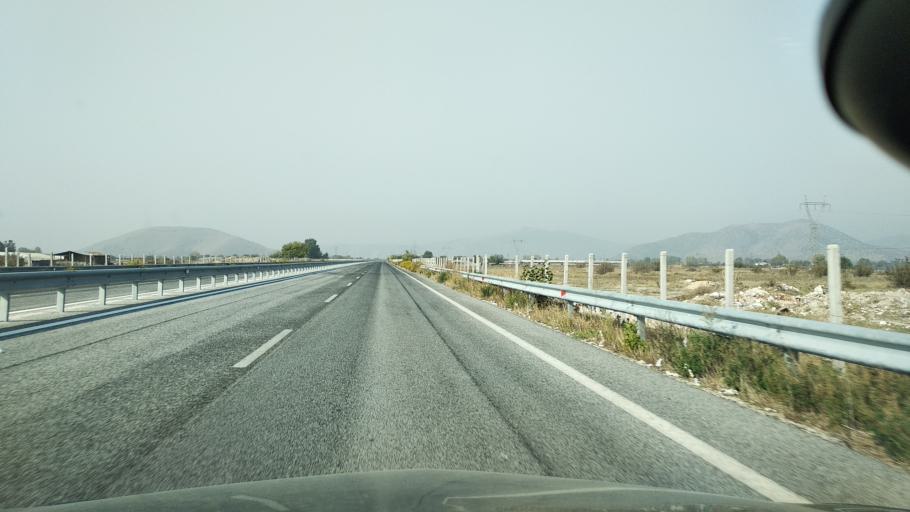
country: GR
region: Thessaly
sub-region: Trikala
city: Farkadona
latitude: 39.5833
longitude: 22.0618
